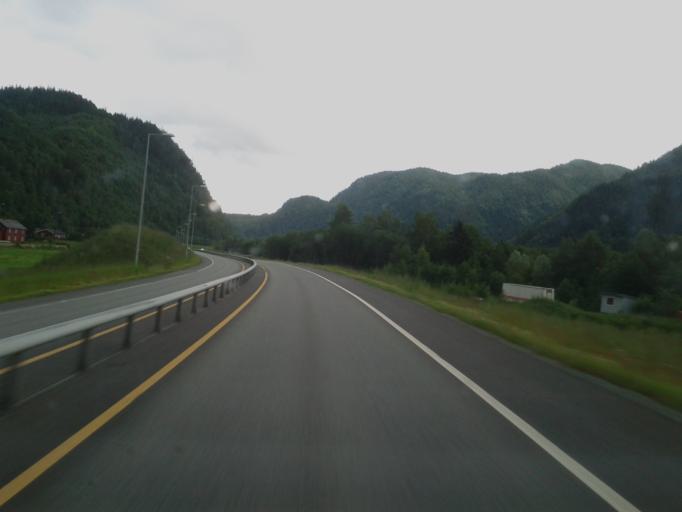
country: NO
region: Sor-Trondelag
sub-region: Midtre Gauldal
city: Storen
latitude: 63.0847
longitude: 10.2512
